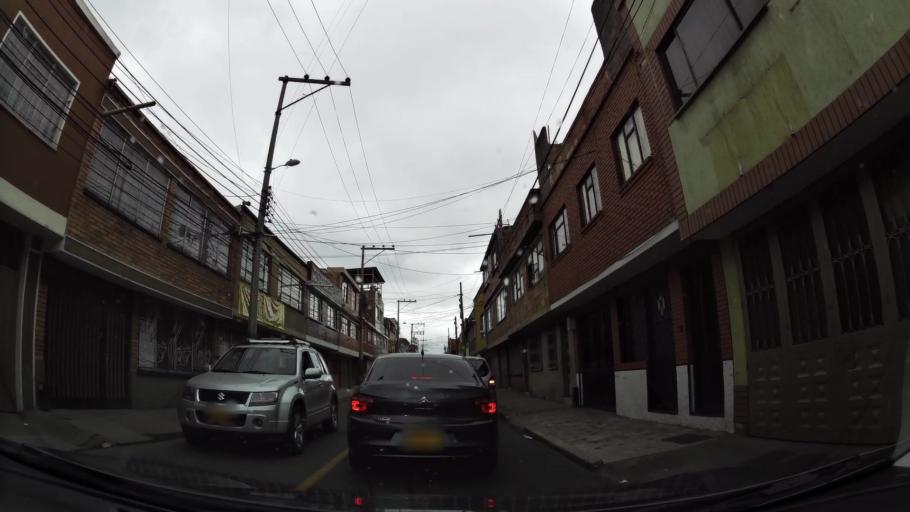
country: CO
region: Bogota D.C.
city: Bogota
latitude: 4.6715
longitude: -74.0978
